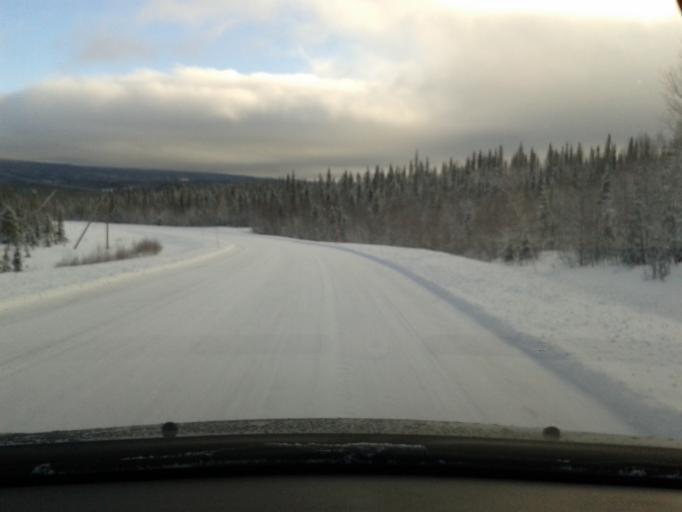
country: SE
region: Vaesterbotten
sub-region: Vilhelmina Kommun
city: Sjoberg
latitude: 65.2568
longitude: 15.6676
